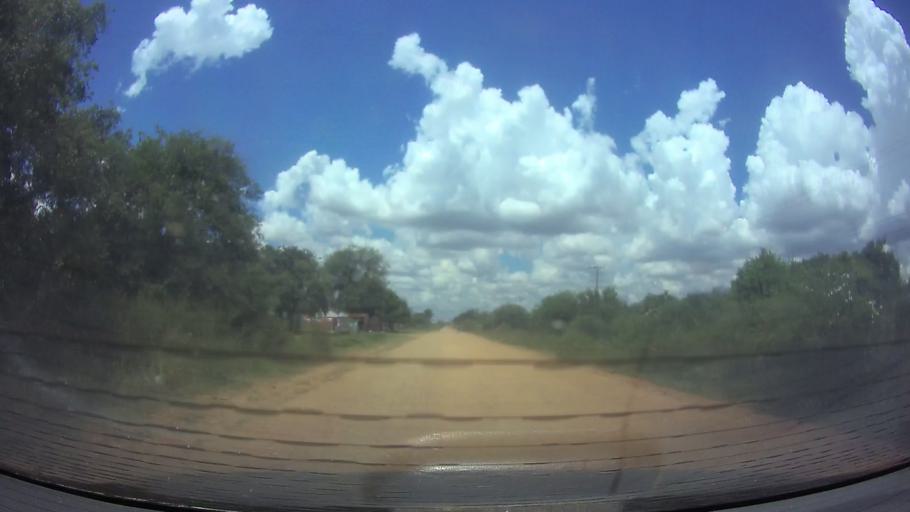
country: PY
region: Presidente Hayes
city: Nanawa
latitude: -25.2510
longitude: -57.6469
